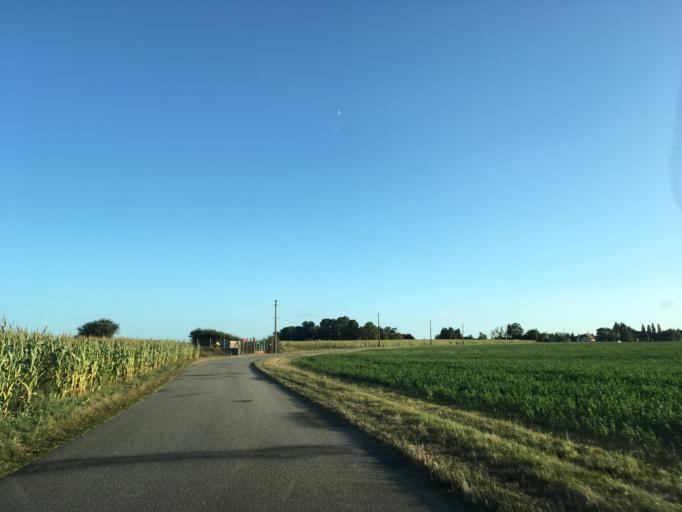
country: FR
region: Haute-Normandie
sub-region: Departement de l'Eure
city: Houlbec-Cocherel
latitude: 49.0592
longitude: 1.3620
